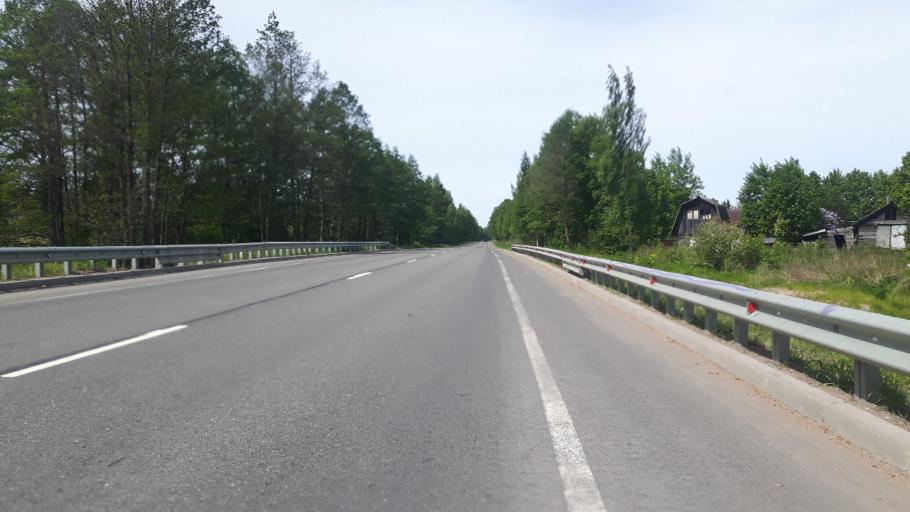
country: RU
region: Leningrad
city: Ust'-Luga
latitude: 59.6516
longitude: 28.3568
